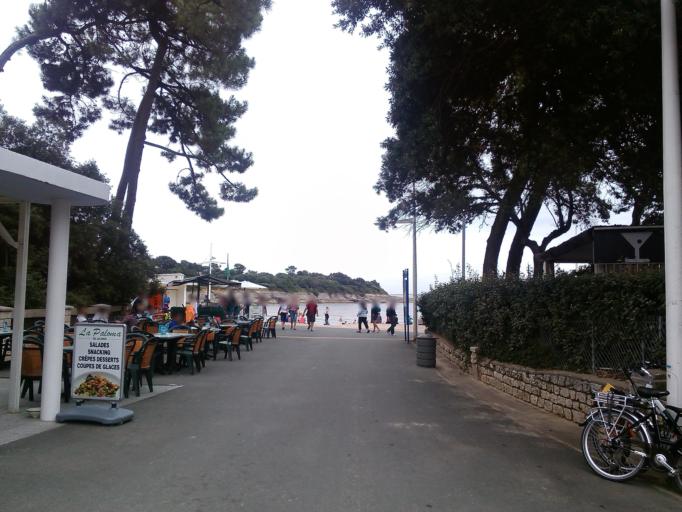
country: FR
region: Poitou-Charentes
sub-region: Departement de la Charente-Maritime
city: Saint-Palais-sur-Mer
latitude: 45.6393
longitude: -1.0780
